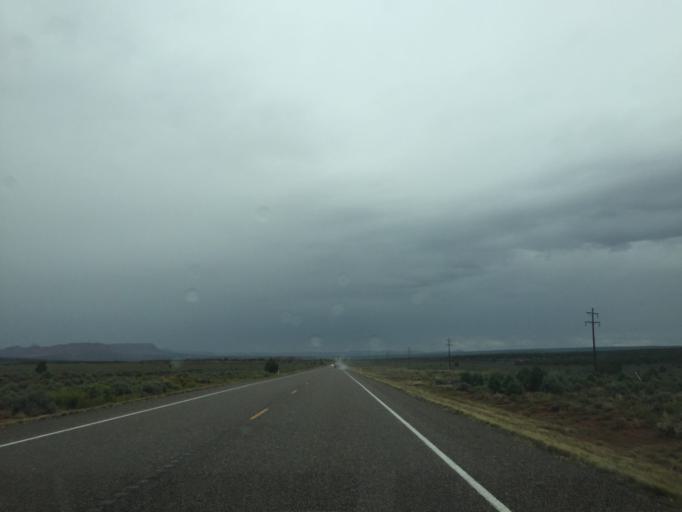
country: US
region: Utah
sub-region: Kane County
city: Kanab
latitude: 37.0901
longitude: -112.1473
